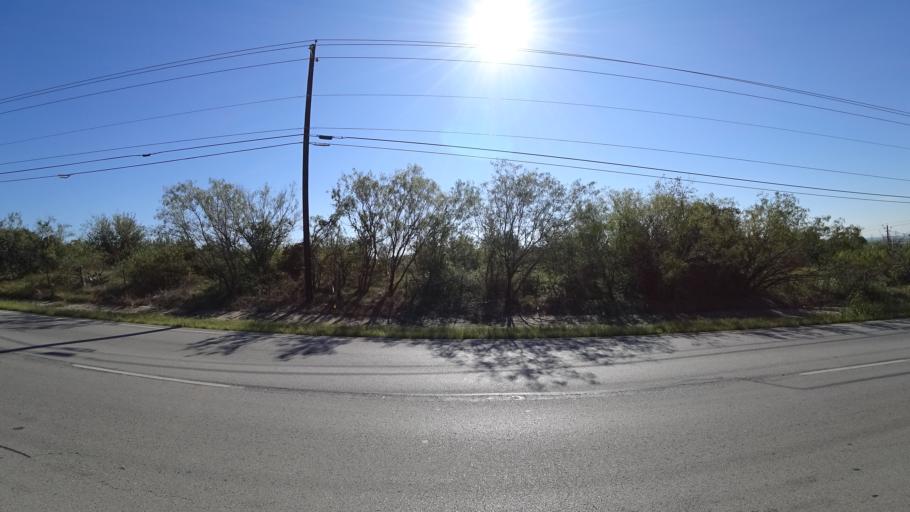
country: US
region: Texas
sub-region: Travis County
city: Hornsby Bend
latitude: 30.2581
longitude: -97.6112
